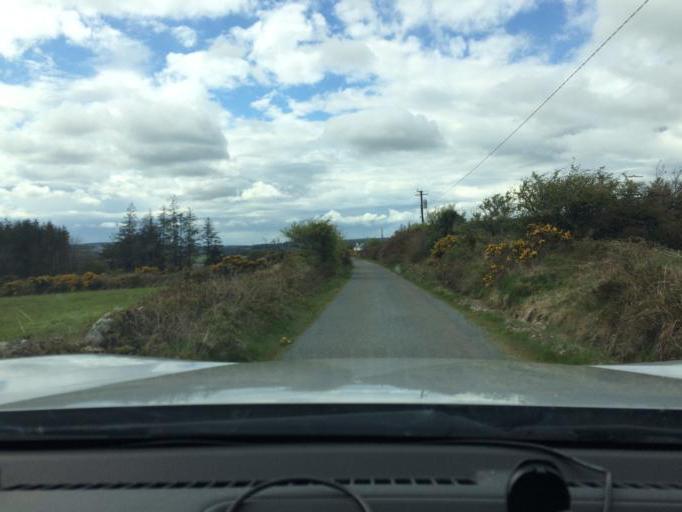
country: IE
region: Munster
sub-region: Waterford
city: Dungarvan
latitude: 52.0409
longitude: -7.6347
